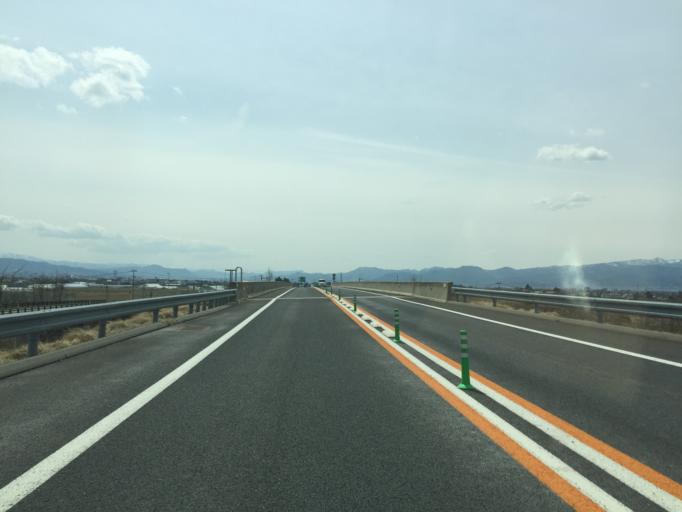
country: JP
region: Yamagata
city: Tendo
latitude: 38.3278
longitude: 140.3280
